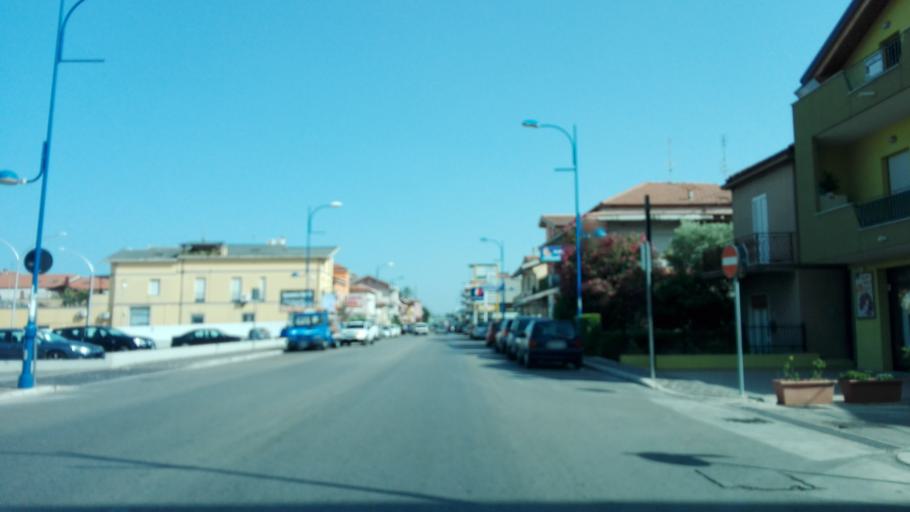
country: IT
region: Abruzzo
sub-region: Provincia di Pescara
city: Montesilvano Marina
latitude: 42.4987
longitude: 14.1714
